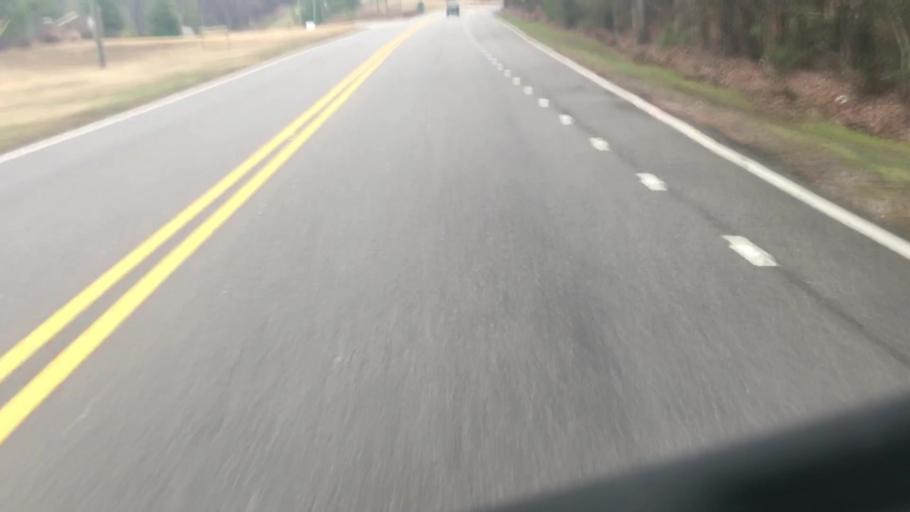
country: US
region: Alabama
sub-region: Jefferson County
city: Hoover
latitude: 33.3564
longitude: -86.8074
